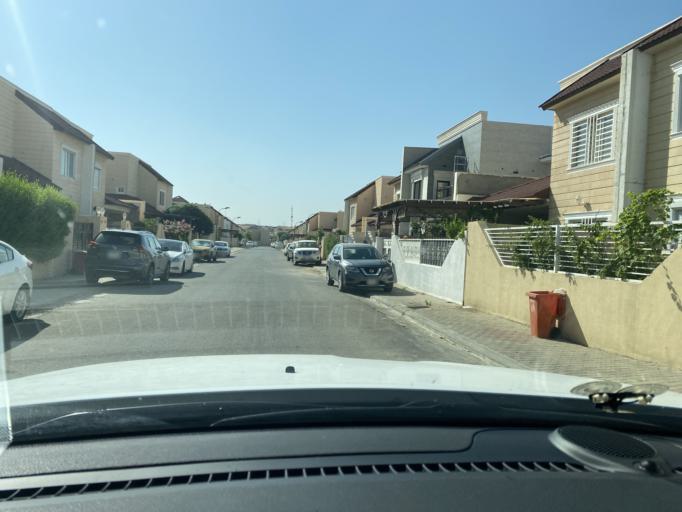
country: IQ
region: Arbil
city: Erbil
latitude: 36.2439
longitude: 44.0489
